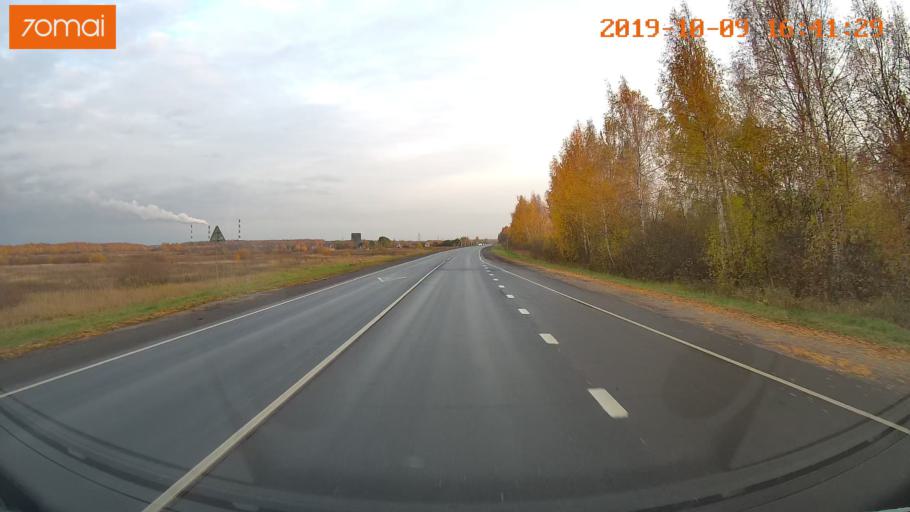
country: RU
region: Kostroma
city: Volgorechensk
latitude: 57.4726
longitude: 41.0820
